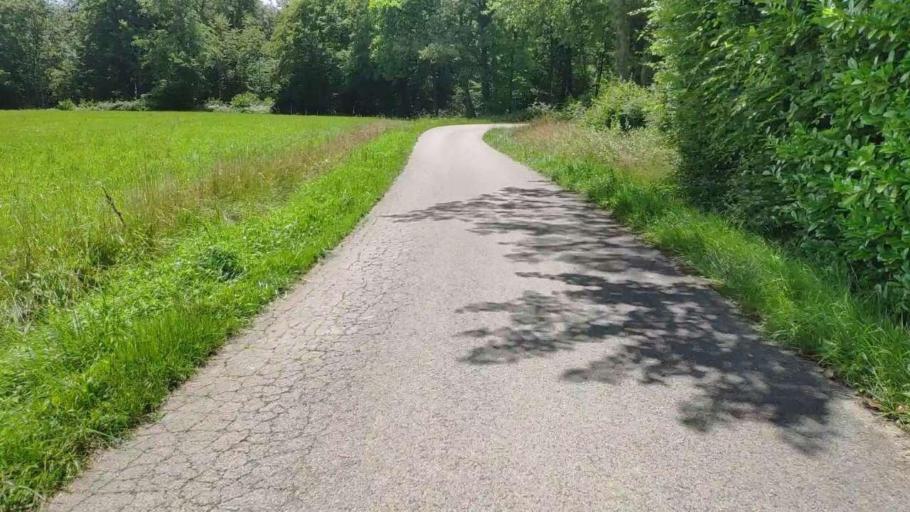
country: FR
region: Franche-Comte
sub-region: Departement du Jura
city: Bletterans
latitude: 46.8395
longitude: 5.4812
